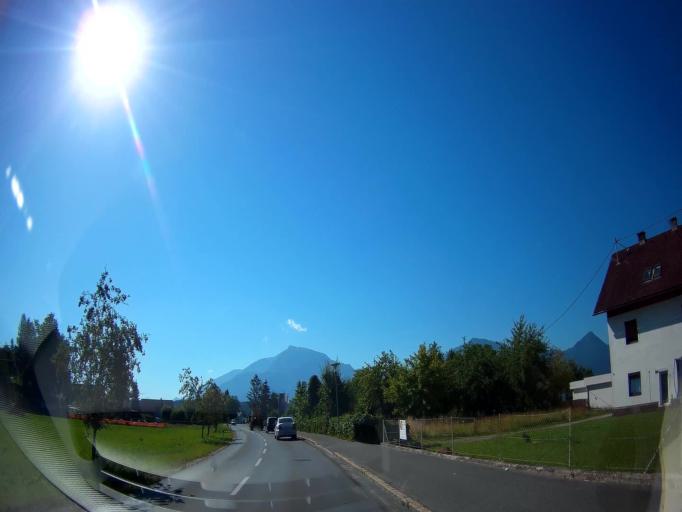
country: AT
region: Carinthia
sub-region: Politischer Bezirk Volkermarkt
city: Eberndorf
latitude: 46.5875
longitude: 14.6470
